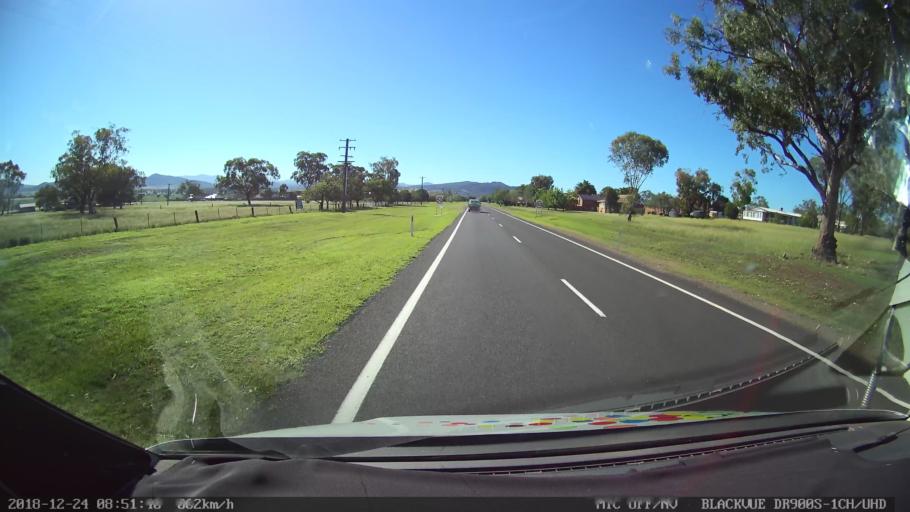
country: AU
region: New South Wales
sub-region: Liverpool Plains
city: Quirindi
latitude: -31.4864
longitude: 150.6755
